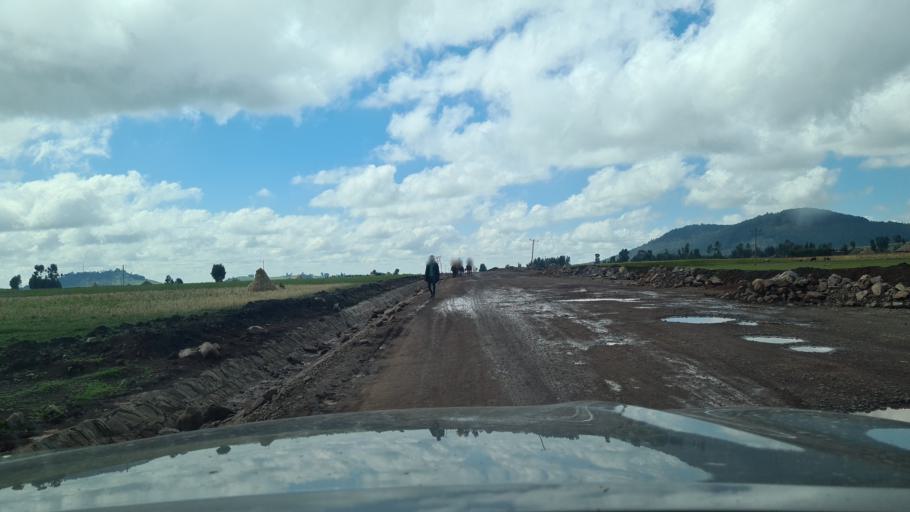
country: ET
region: Oromiya
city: Huruta
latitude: 8.0933
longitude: 39.5363
